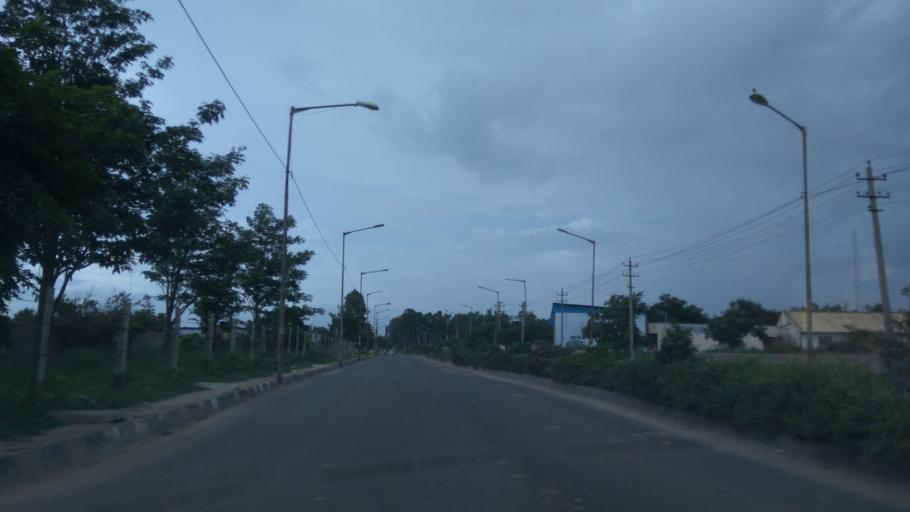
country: IN
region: Karnataka
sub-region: Bangalore Urban
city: Yelahanka
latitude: 13.0918
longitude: 77.6358
